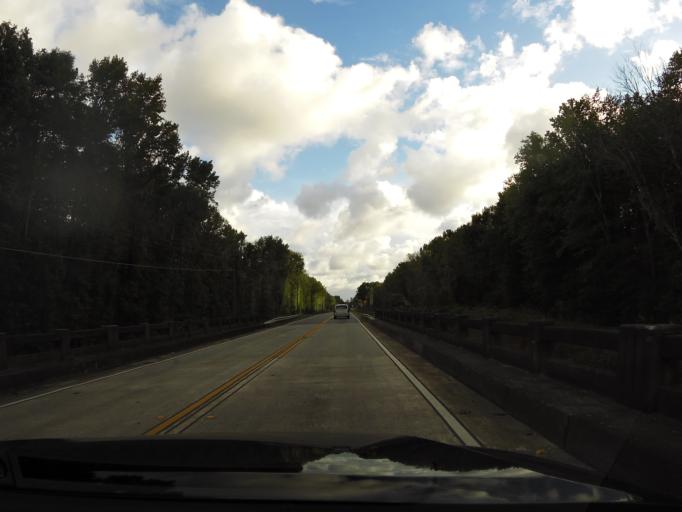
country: US
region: Georgia
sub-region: Liberty County
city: Midway
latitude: 31.8208
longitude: -81.4298
